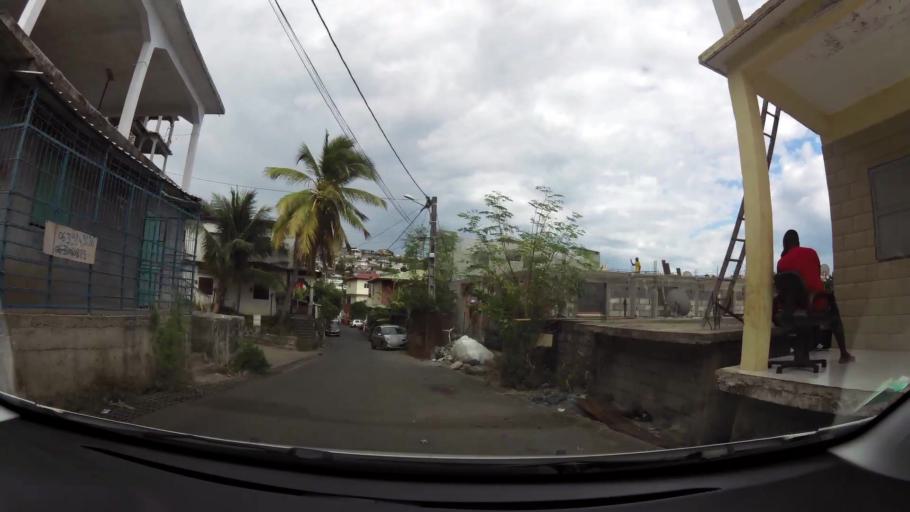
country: YT
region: Sada
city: Sada
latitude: -12.8498
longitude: 45.0999
